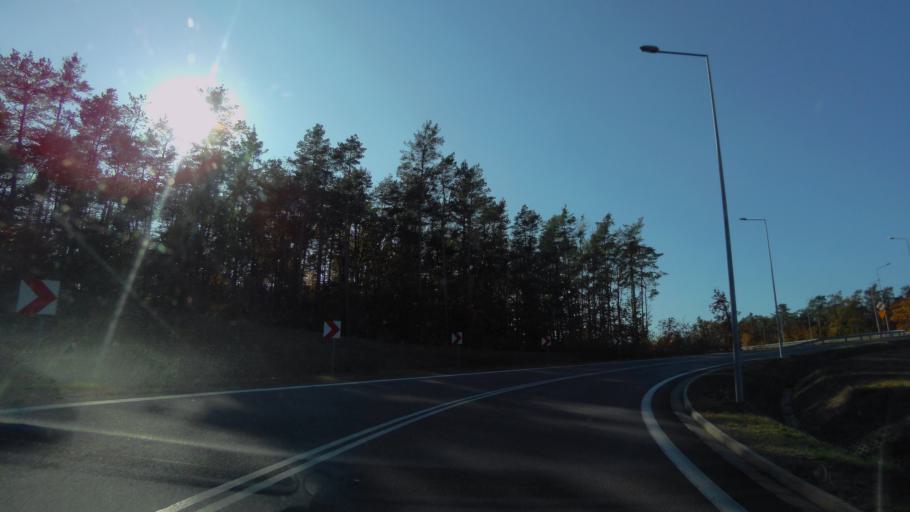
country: PL
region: Subcarpathian Voivodeship
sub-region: Powiat lezajski
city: Lezajsk
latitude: 50.2749
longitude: 22.3987
